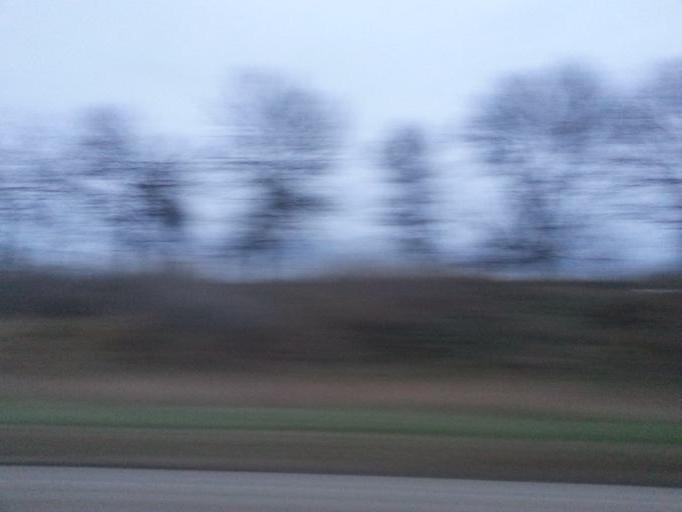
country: US
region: Iowa
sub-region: Buchanan County
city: Jesup
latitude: 42.3424
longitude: -92.0336
